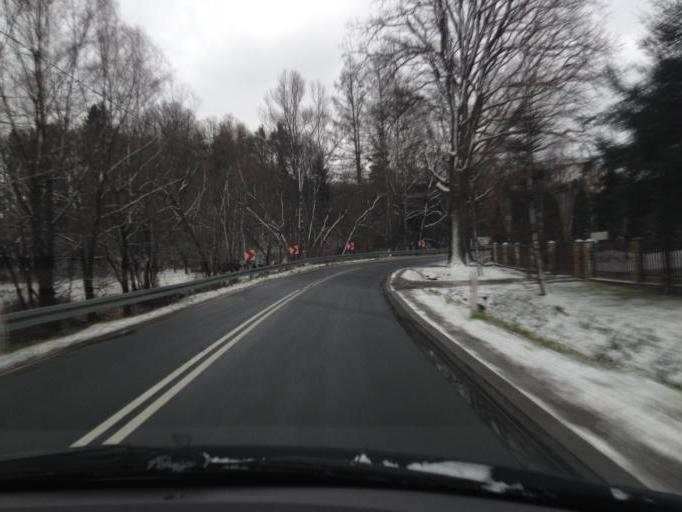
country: PL
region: Lesser Poland Voivodeship
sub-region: Powiat tarnowski
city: Rzepiennik Strzyzewski
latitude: 49.8226
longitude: 21.0084
